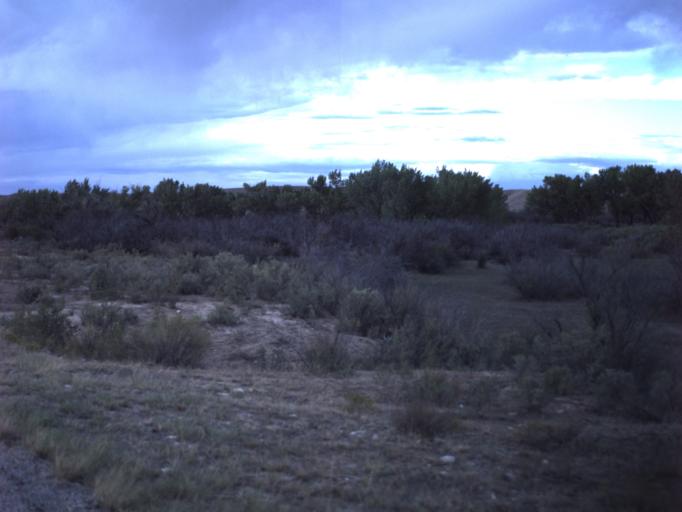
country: US
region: Utah
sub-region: Grand County
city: Moab
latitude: 38.8566
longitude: -109.2894
